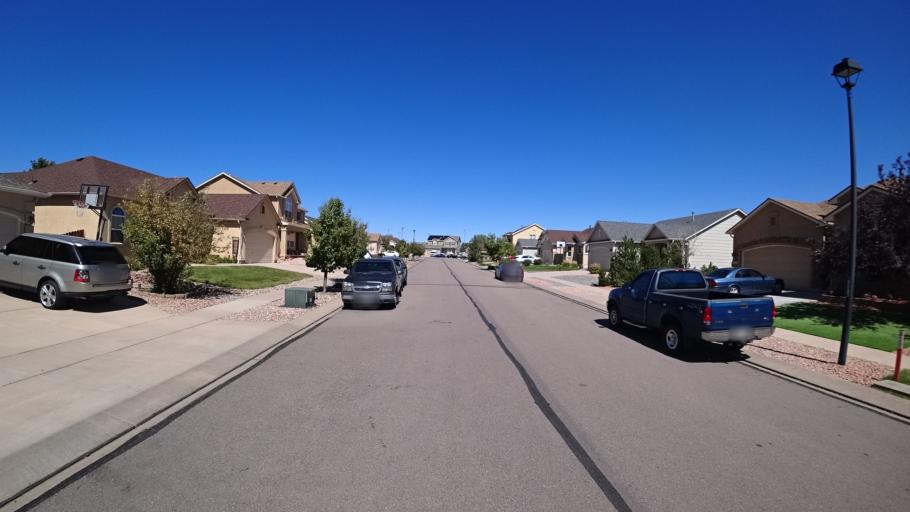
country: US
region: Colorado
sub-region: El Paso County
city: Security-Widefield
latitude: 38.7841
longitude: -104.7261
